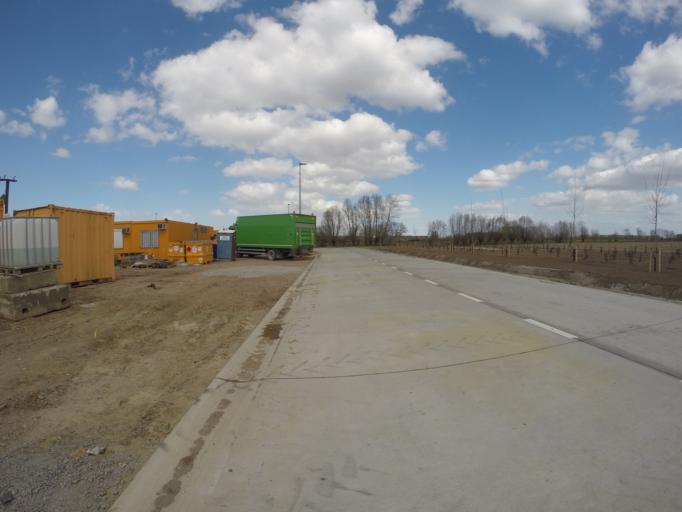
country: BE
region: Flanders
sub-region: Provincie Oost-Vlaanderen
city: Aalter
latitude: 51.1120
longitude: 3.4523
